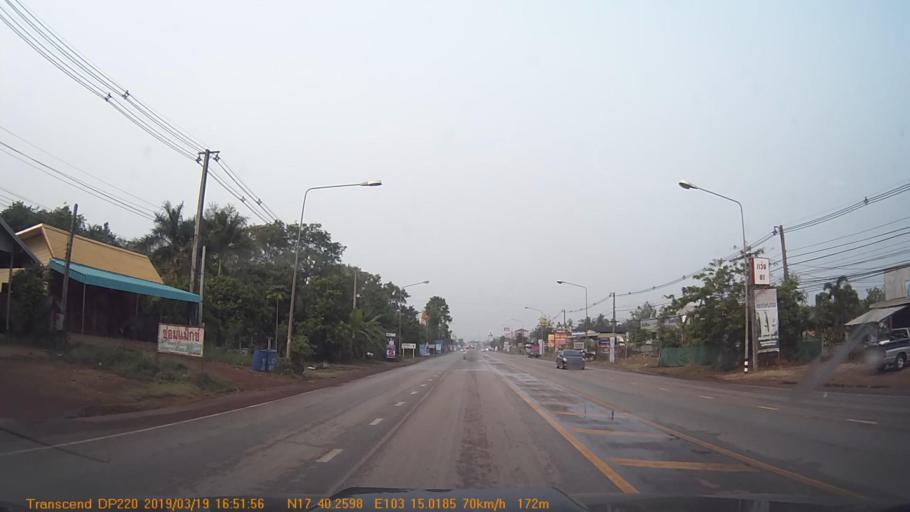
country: TH
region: Changwat Udon Thani
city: Ban Dung
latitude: 17.6714
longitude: 103.2505
